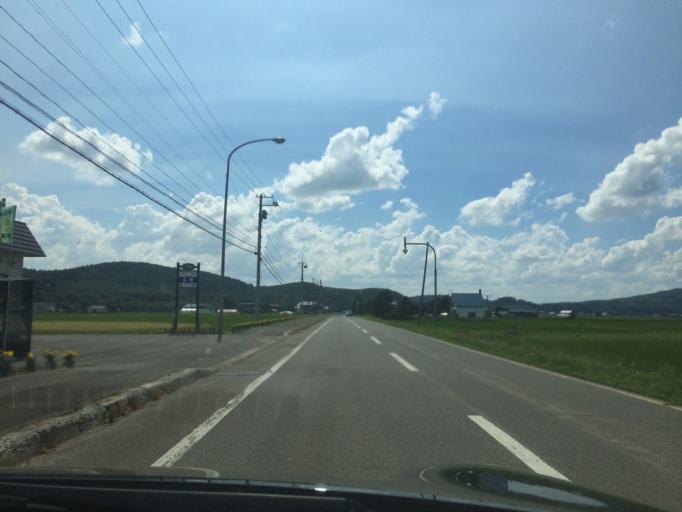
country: JP
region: Hokkaido
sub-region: Asahikawa-shi
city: Asahikawa
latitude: 43.7545
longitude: 142.5281
